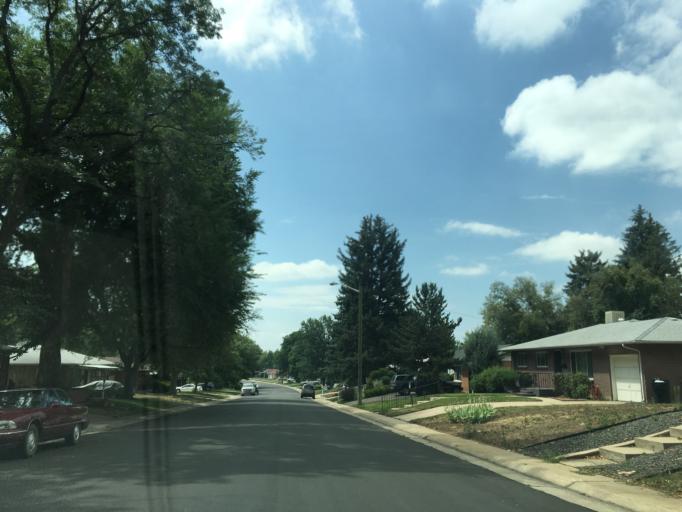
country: US
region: Colorado
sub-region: Arapahoe County
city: Sheridan
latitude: 39.6618
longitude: -105.0521
